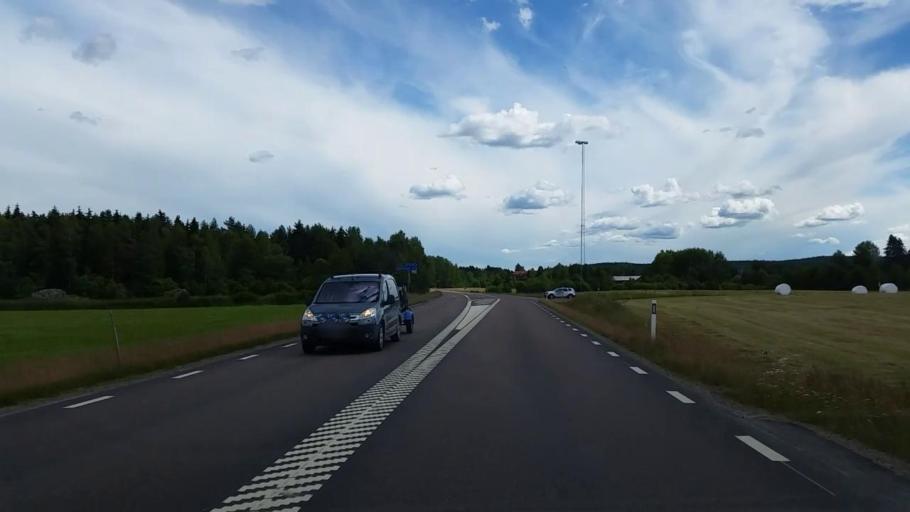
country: SE
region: Gaevleborg
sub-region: Ovanakers Kommun
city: Edsbyn
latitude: 61.3725
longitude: 15.8477
